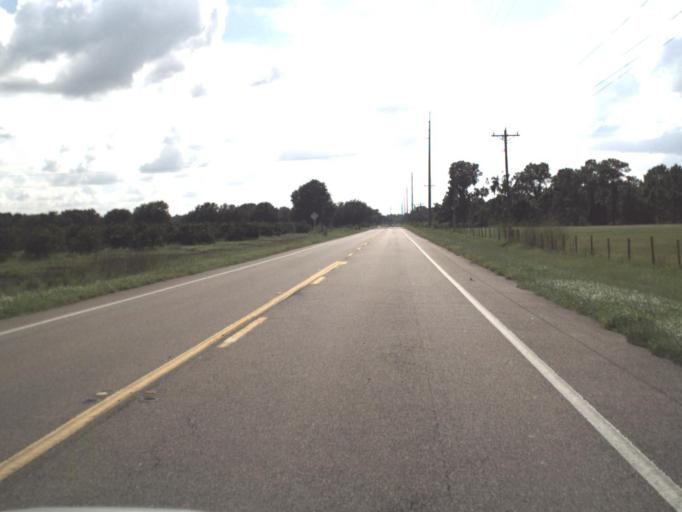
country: US
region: Florida
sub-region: Hardee County
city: Wauchula
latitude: 27.4834
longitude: -82.0443
